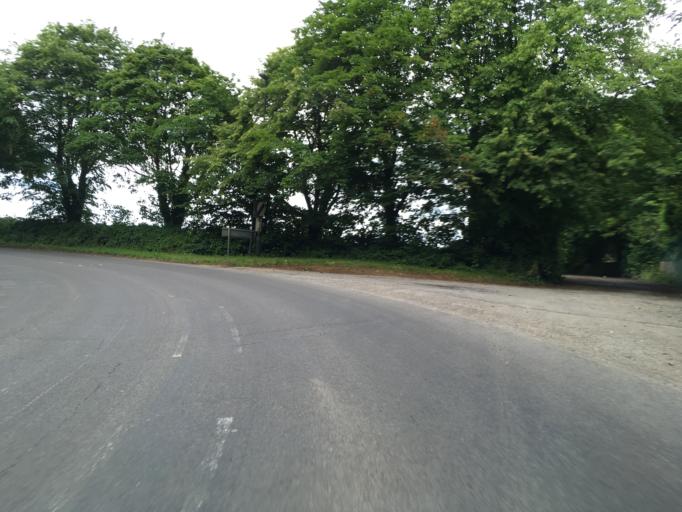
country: GB
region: England
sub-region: Oxfordshire
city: Shipton under Wychwood
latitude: 51.8543
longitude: -1.6013
